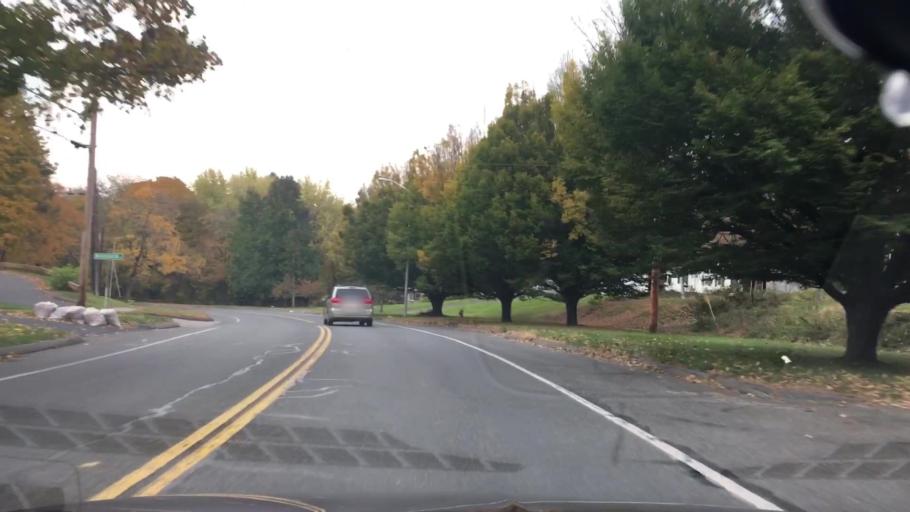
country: US
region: Massachusetts
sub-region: Hampden County
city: Longmeadow
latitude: 42.0282
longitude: -72.5814
